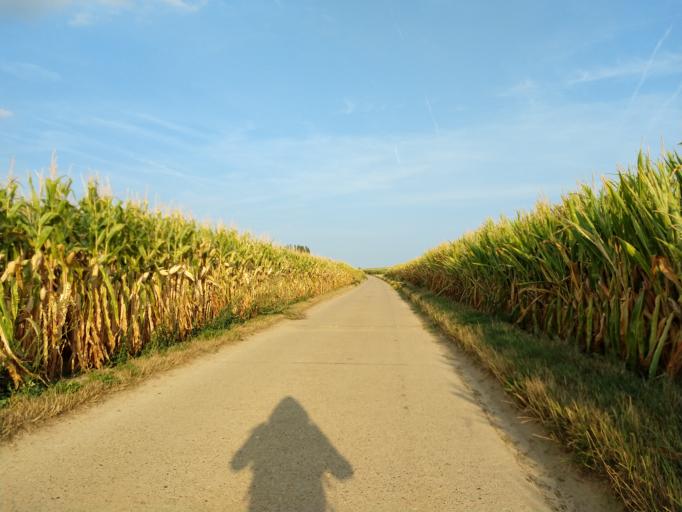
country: BE
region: Flanders
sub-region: Provincie Vlaams-Brabant
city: Boutersem
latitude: 50.8128
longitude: 4.8252
